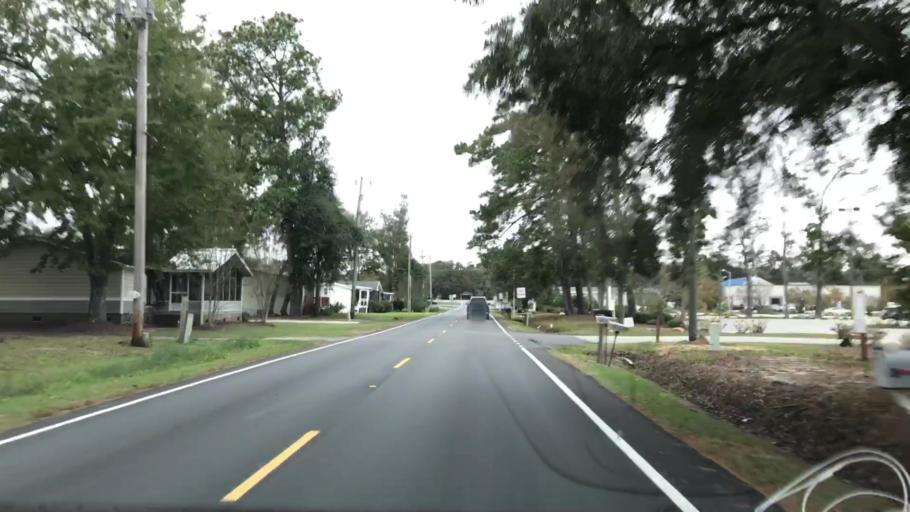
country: US
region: South Carolina
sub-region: Horry County
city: Garden City
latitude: 33.5885
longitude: -79.0041
